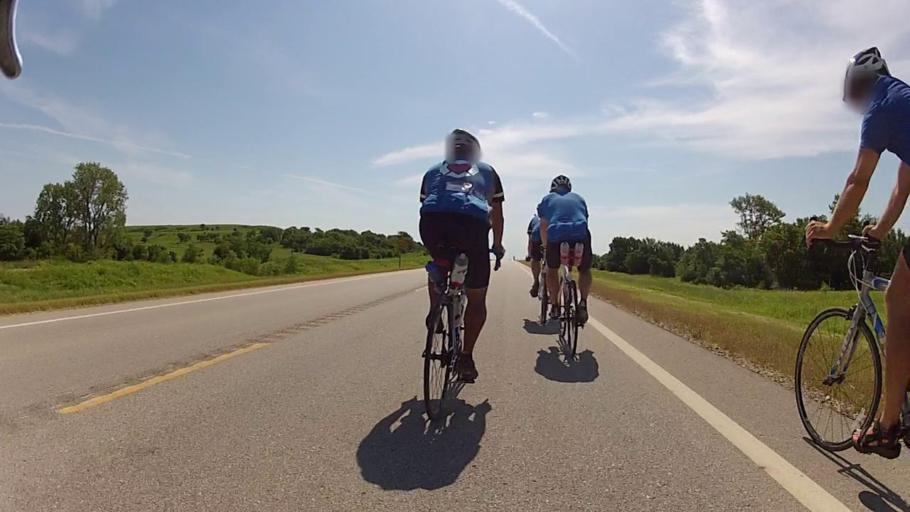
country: US
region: Kansas
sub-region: Chautauqua County
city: Sedan
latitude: 37.1071
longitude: -96.5751
